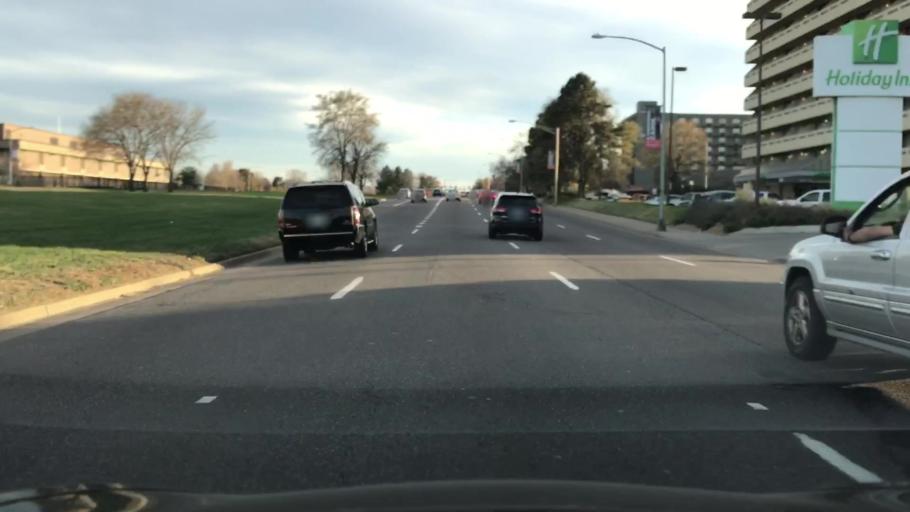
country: US
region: Colorado
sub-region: Adams County
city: Commerce City
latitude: 39.7650
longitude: -104.9034
